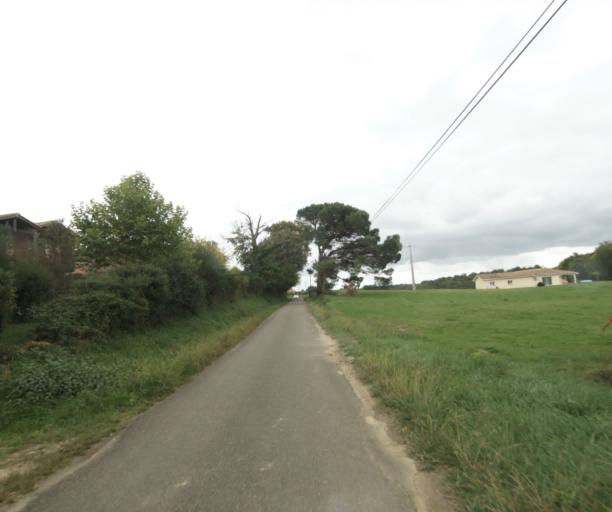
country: FR
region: Midi-Pyrenees
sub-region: Departement du Gers
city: Eauze
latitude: 43.8982
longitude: 0.1141
